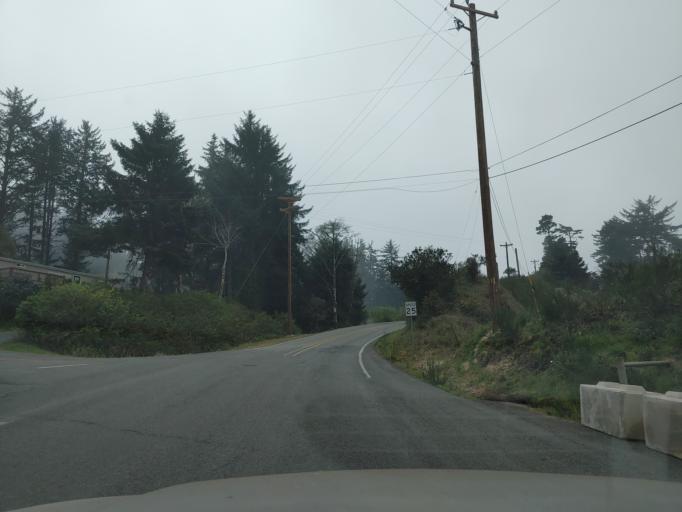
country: US
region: Oregon
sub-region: Coos County
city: Lakeside
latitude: 43.6667
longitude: -124.1962
